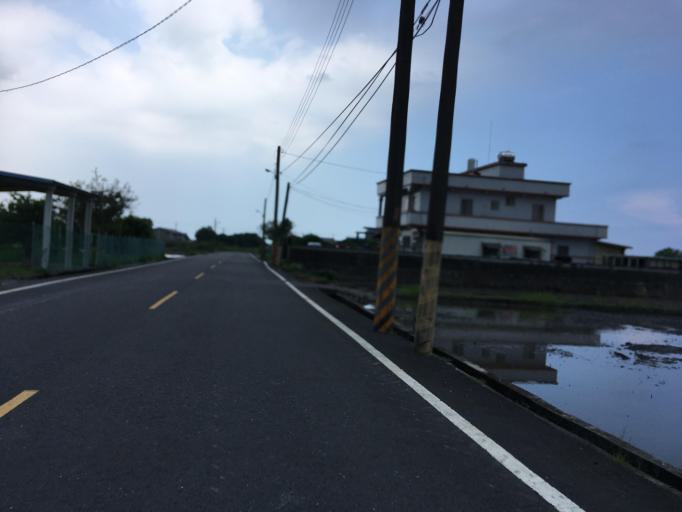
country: TW
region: Taiwan
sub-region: Yilan
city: Yilan
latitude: 24.6837
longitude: 121.7050
